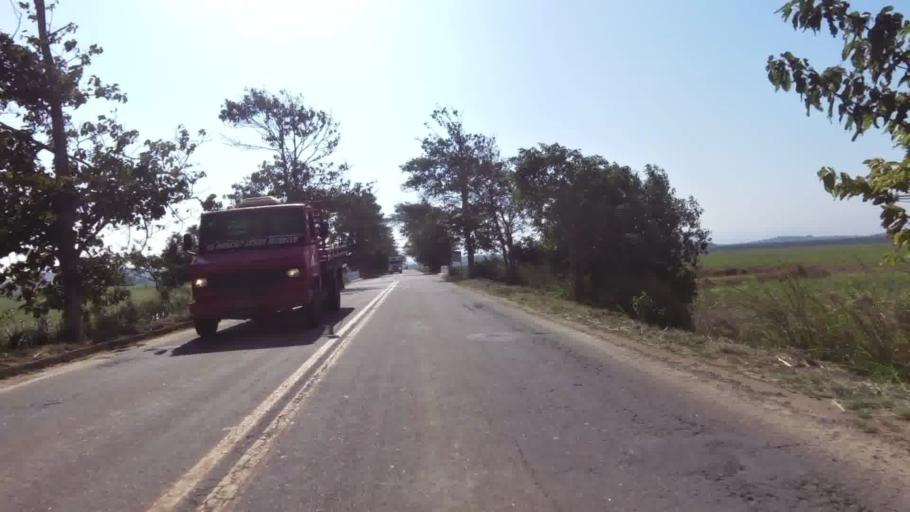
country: BR
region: Espirito Santo
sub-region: Itapemirim
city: Itapemirim
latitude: -20.9909
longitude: -40.8534
